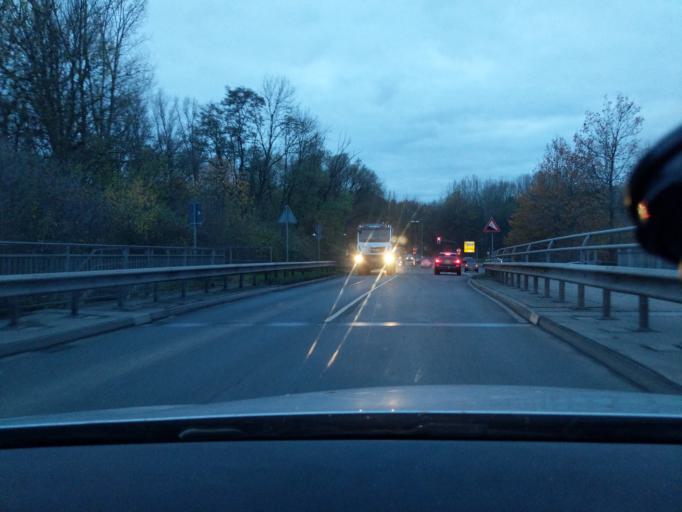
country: DE
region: North Rhine-Westphalia
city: Lunen
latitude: 51.6053
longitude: 7.4789
